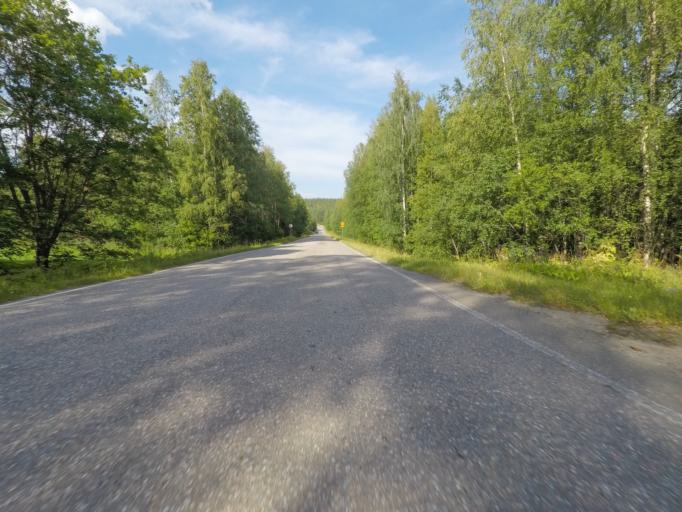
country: FI
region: Southern Savonia
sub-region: Mikkeli
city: Puumala
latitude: 61.6765
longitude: 28.2265
